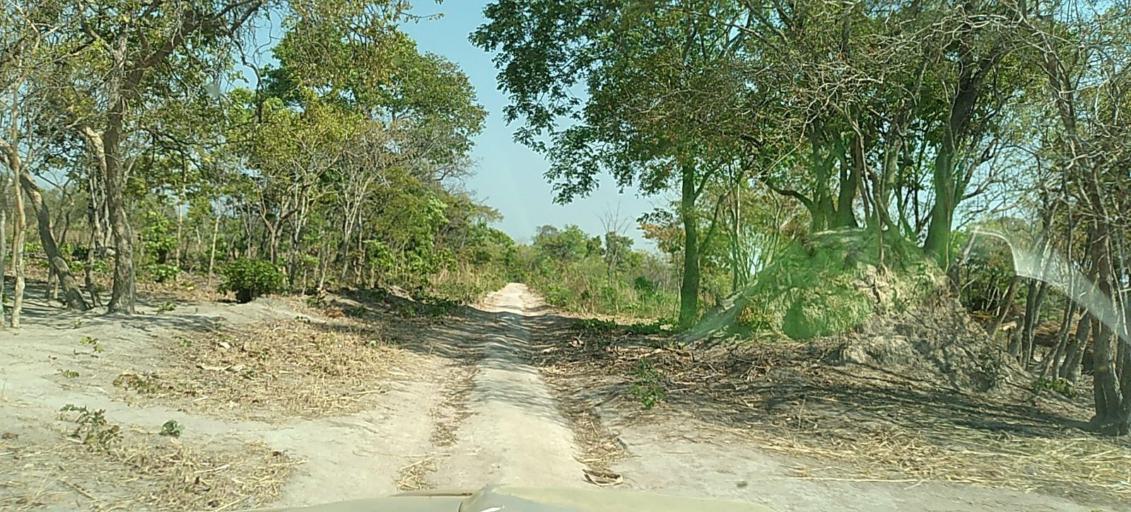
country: ZM
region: North-Western
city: Kalengwa
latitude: -13.3152
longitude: 24.8145
